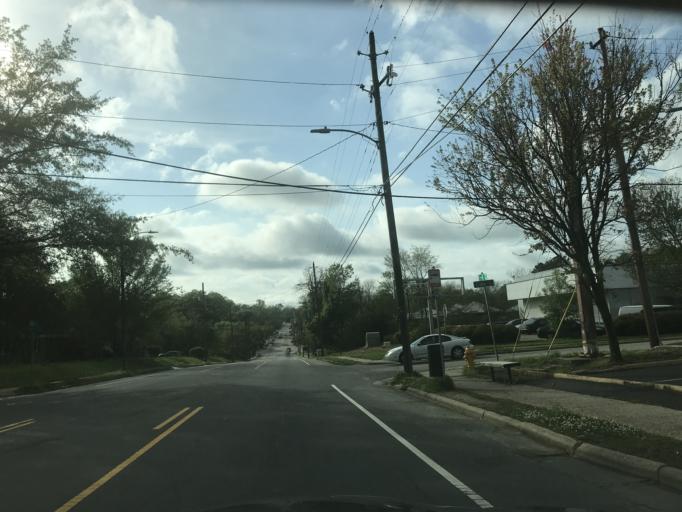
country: US
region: North Carolina
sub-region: Wake County
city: Raleigh
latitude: 35.7768
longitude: -78.6115
